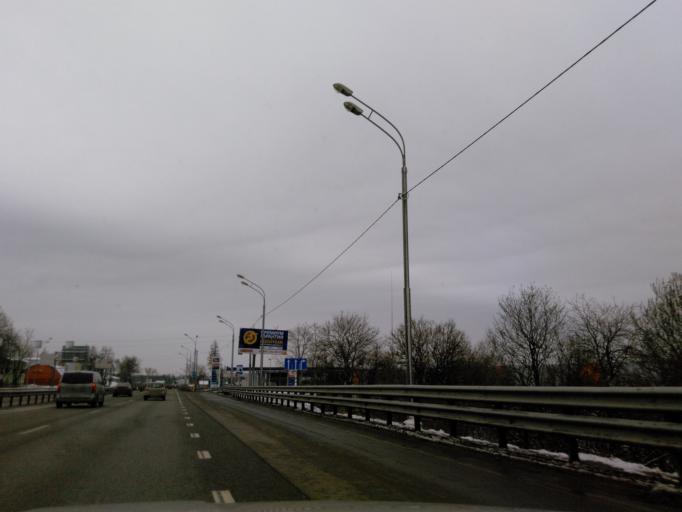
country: RU
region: Moskovskaya
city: Skhodnya
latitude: 55.9773
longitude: 37.3018
